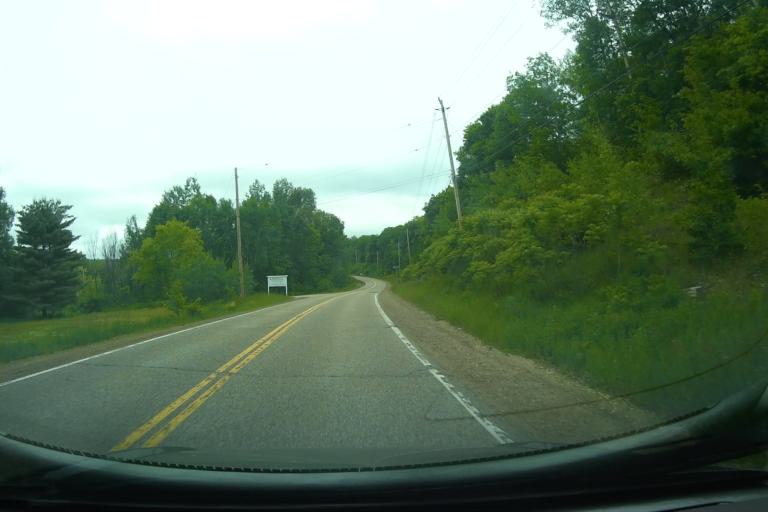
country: CA
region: Ontario
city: Pembroke
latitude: 45.4667
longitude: -77.2237
